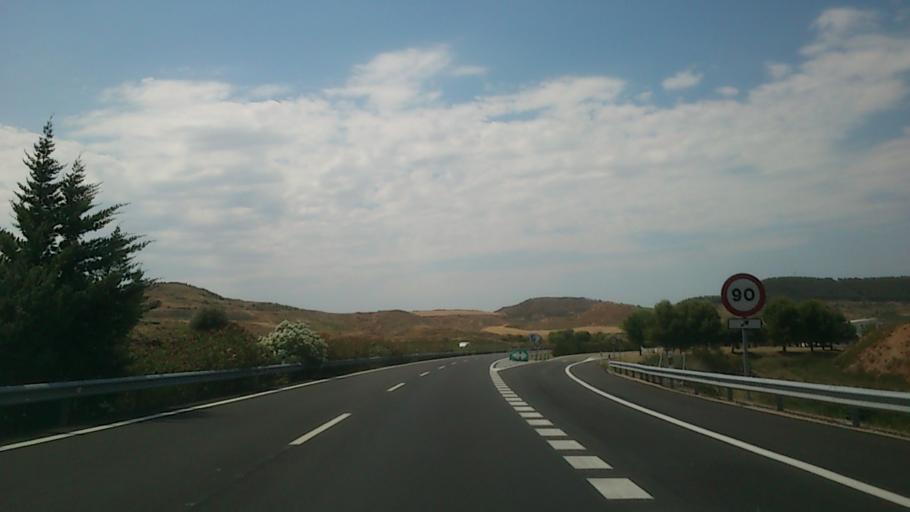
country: ES
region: La Rioja
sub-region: Provincia de La Rioja
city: Fuenmayor
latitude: 42.4580
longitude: -2.5927
